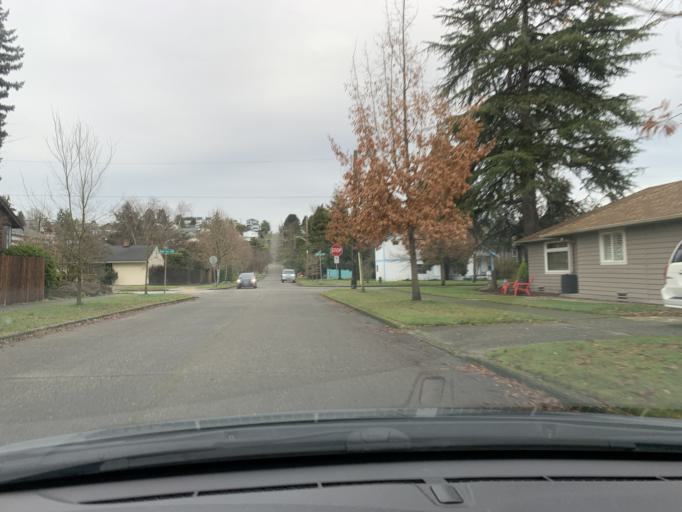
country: US
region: Washington
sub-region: King County
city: White Center
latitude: 47.5593
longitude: -122.3955
